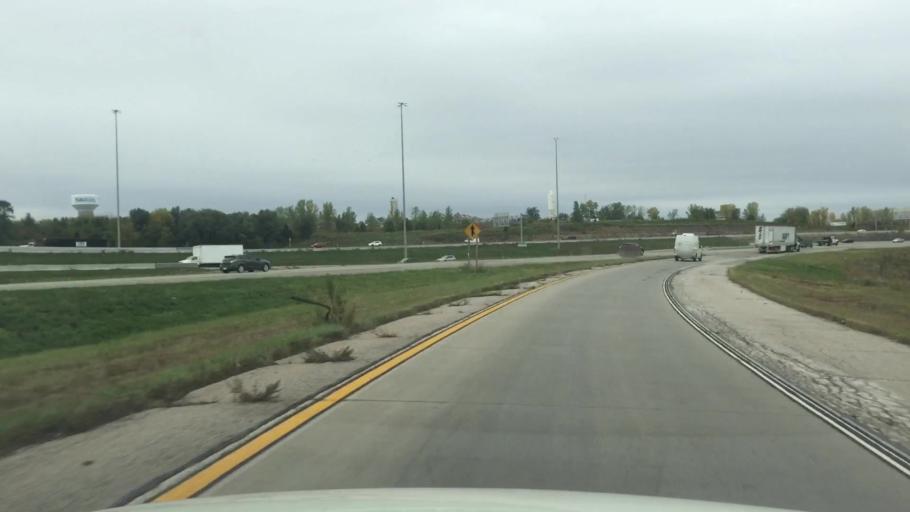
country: US
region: Kansas
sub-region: Johnson County
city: Lenexa
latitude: 38.9440
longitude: -94.7746
